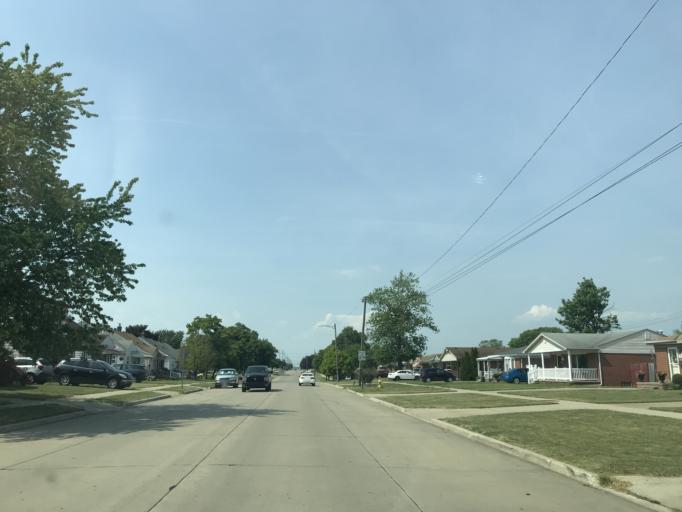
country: US
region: Michigan
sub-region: Wayne County
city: Riverview
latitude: 42.1803
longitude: -83.1794
